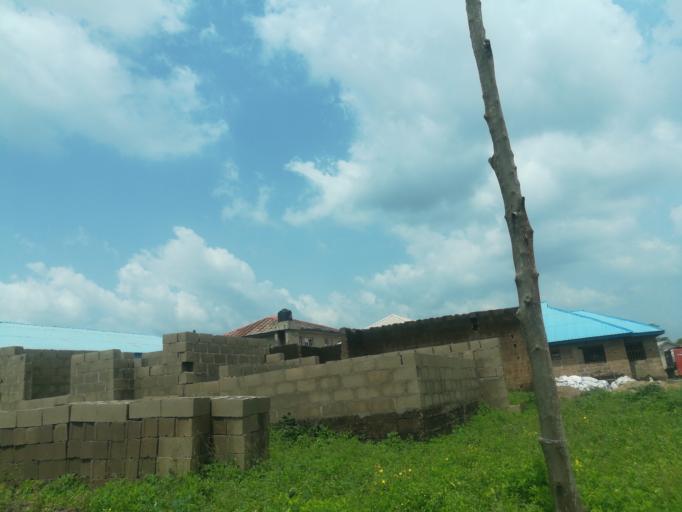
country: NG
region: Oyo
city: Ibadan
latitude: 7.4356
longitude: 3.9357
